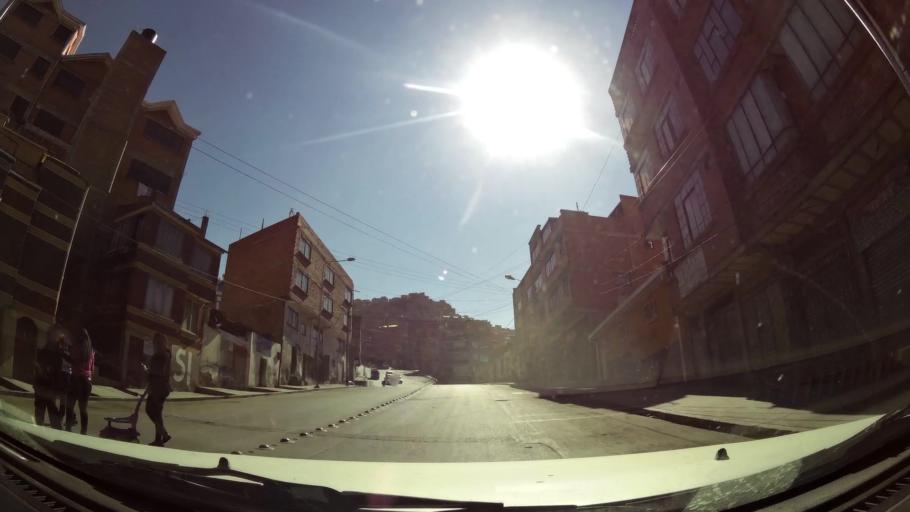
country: BO
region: La Paz
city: La Paz
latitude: -16.5110
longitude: -68.1425
